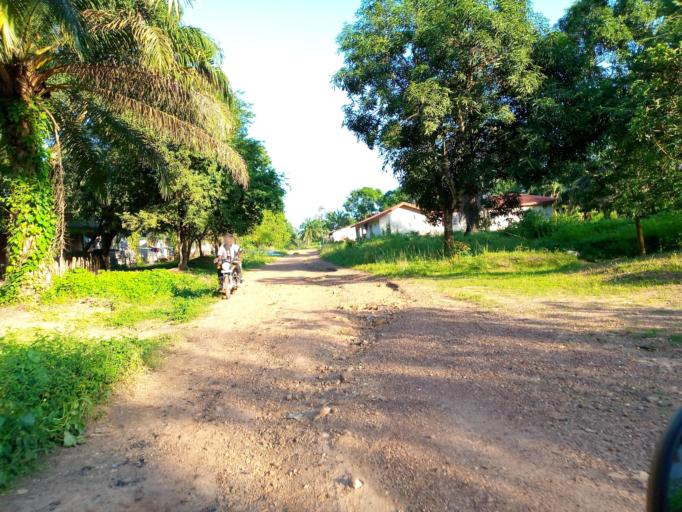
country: SL
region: Northern Province
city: Yonibana
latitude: 8.4463
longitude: -12.2407
